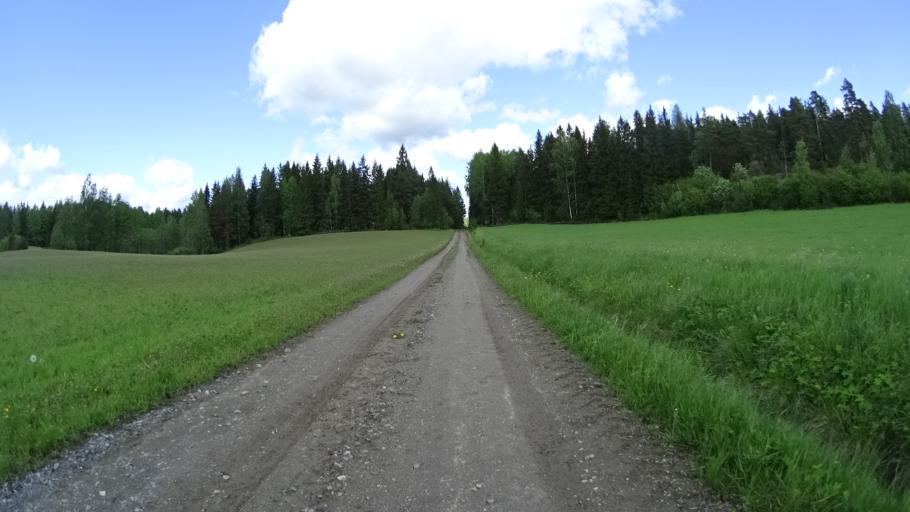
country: FI
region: Uusimaa
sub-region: Raaseporin
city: Karis
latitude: 60.1478
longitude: 23.6221
